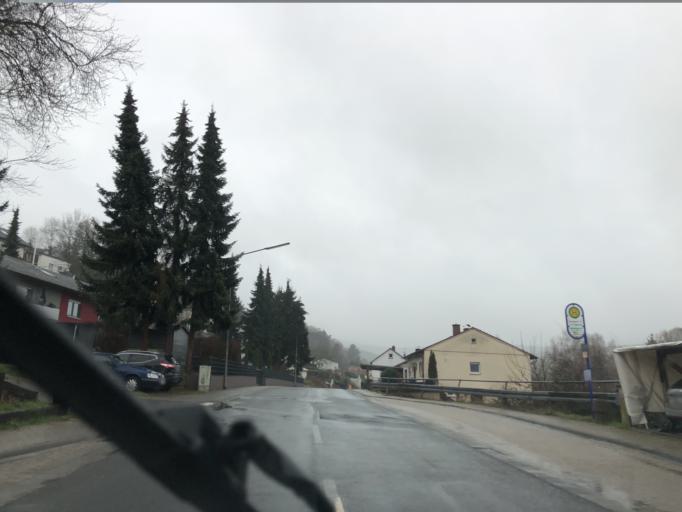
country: DE
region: Hesse
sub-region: Regierungsbezirk Darmstadt
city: Lutzelbach
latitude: 49.7674
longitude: 9.1044
